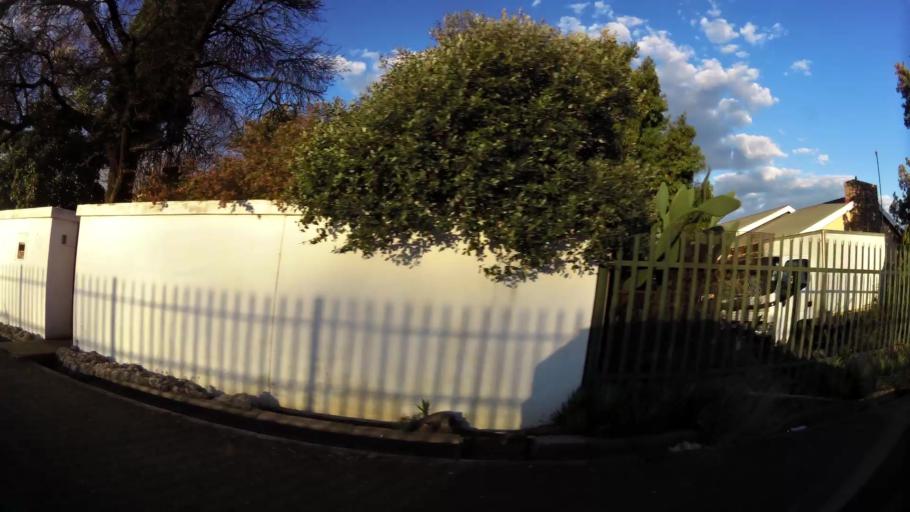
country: ZA
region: North-West
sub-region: Dr Kenneth Kaunda District Municipality
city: Potchefstroom
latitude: -26.7183
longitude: 27.0916
